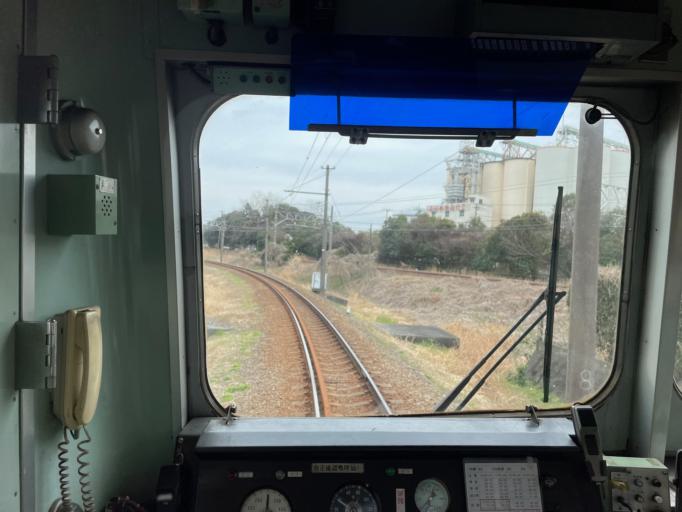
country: JP
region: Shizuoka
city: Fuji
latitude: 35.1462
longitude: 138.6918
